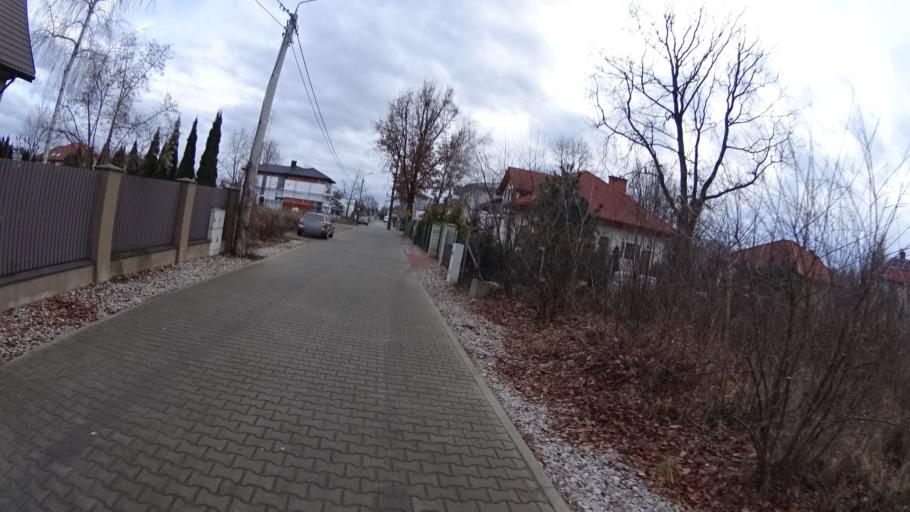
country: PL
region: Masovian Voivodeship
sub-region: Powiat pruszkowski
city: Granica
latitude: 52.1494
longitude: 20.7949
